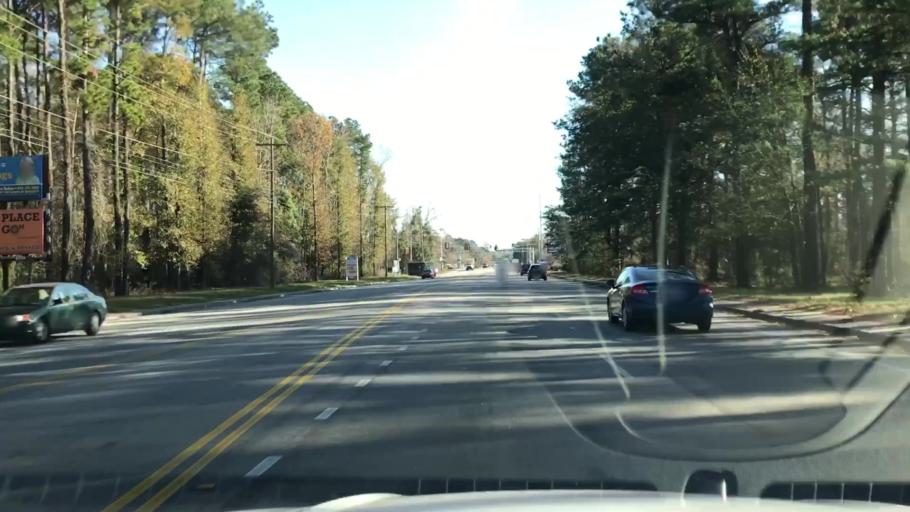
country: US
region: South Carolina
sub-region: Berkeley County
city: Ladson
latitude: 32.9849
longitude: -80.1133
